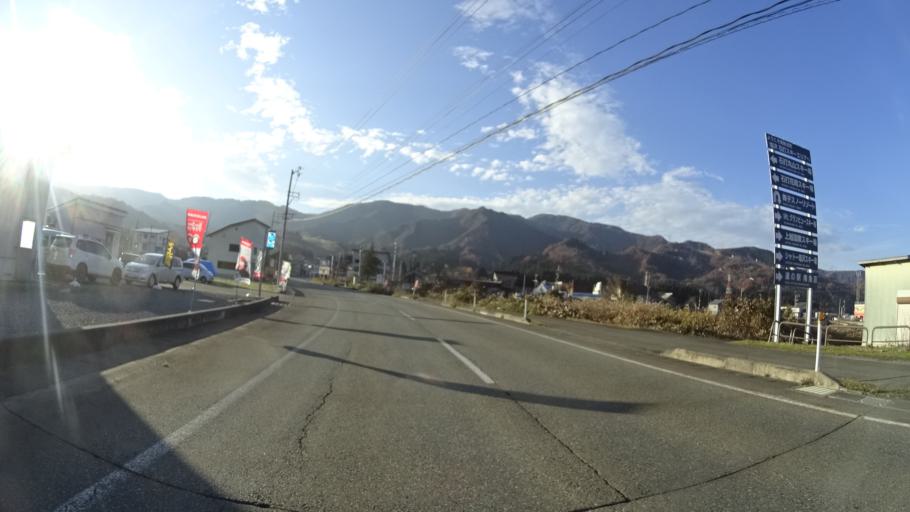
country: JP
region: Niigata
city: Shiozawa
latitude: 36.9894
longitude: 138.8117
